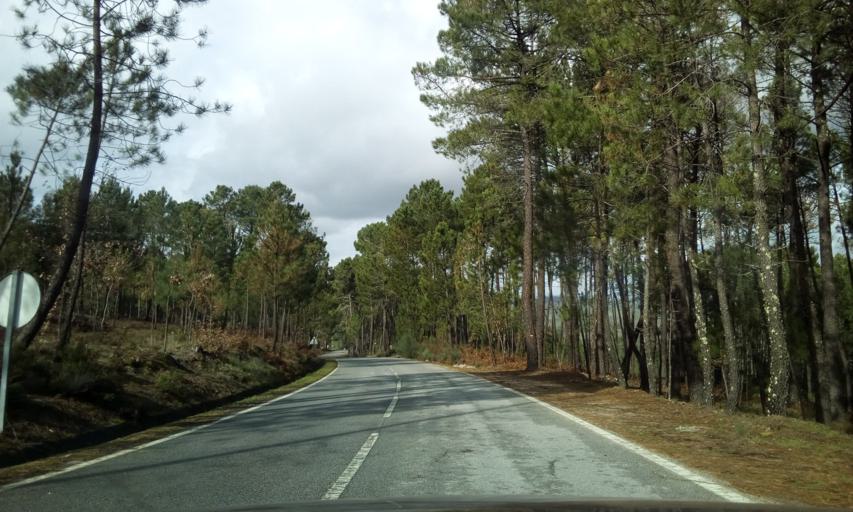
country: PT
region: Guarda
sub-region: Fornos de Algodres
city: Fornos de Algodres
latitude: 40.6617
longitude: -7.6395
